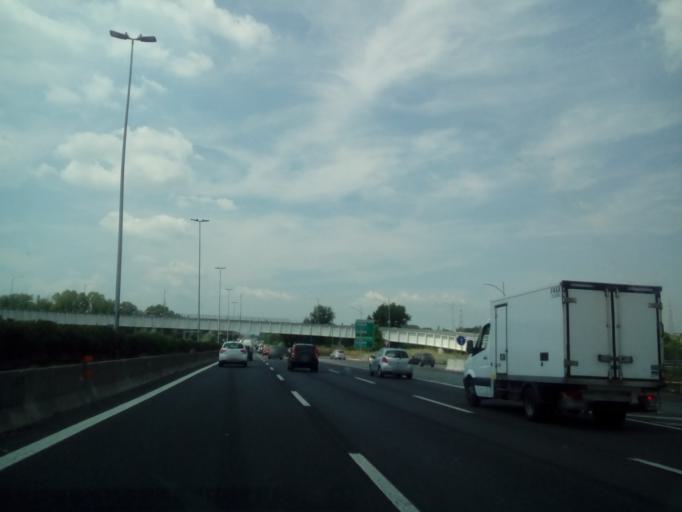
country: IT
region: Latium
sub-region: Citta metropolitana di Roma Capitale
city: Setteville
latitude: 41.9221
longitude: 12.6103
